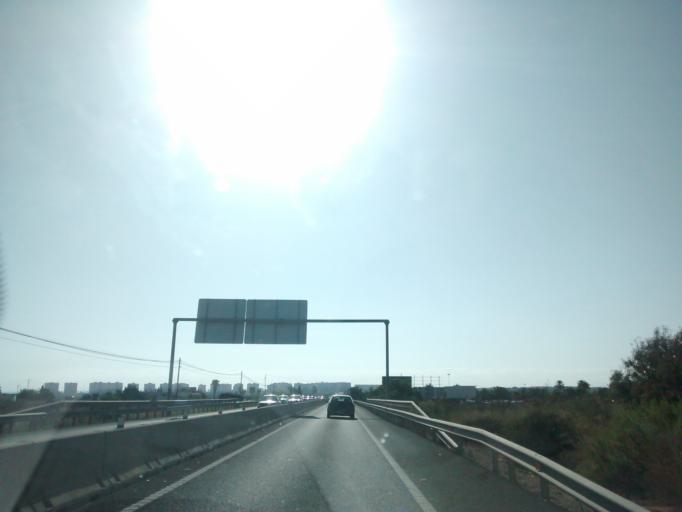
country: ES
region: Valencia
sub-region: Provincia de Alicante
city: Alicante
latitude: 38.2874
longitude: -0.5461
